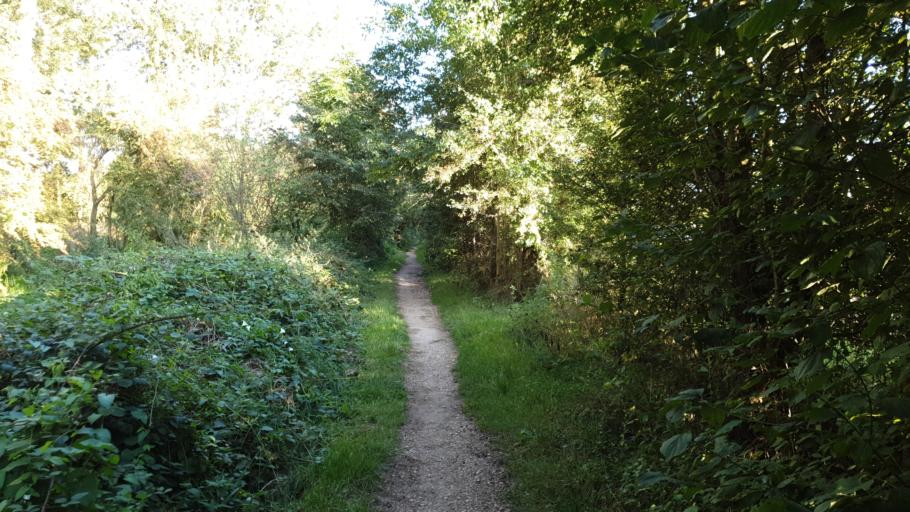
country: GB
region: England
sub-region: Wiltshire
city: Minety
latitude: 51.6465
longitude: -1.9623
